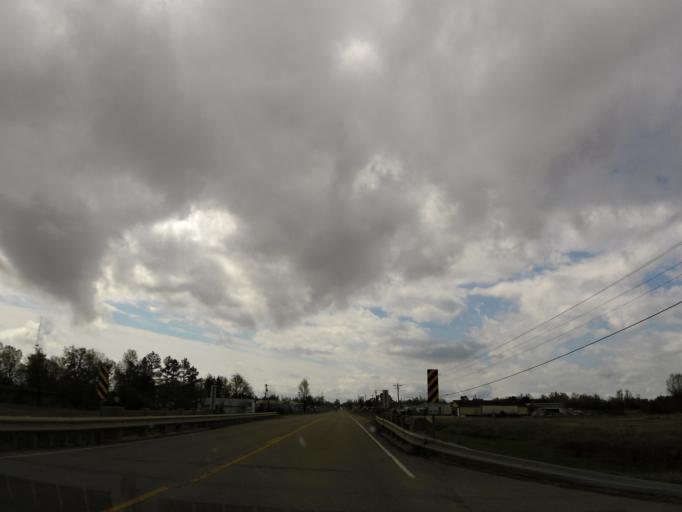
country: US
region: Arkansas
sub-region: Clay County
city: Corning
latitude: 36.4264
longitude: -90.5861
